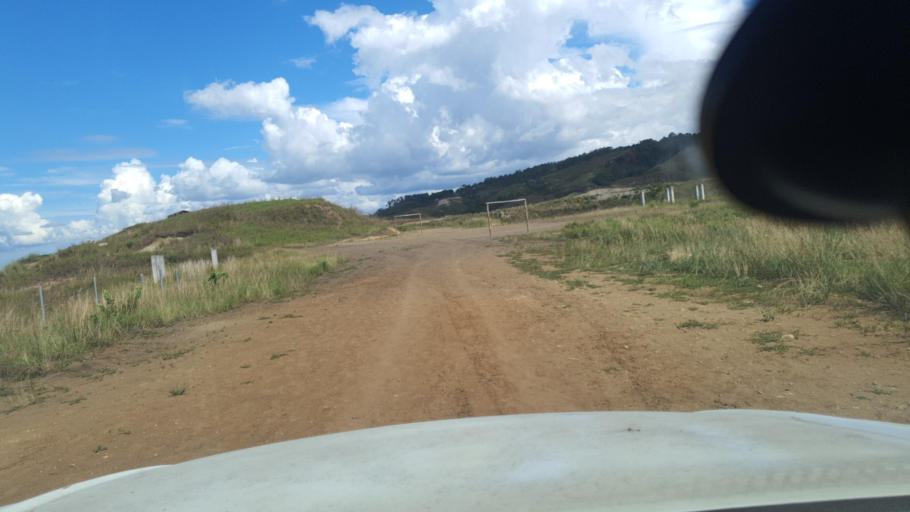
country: SB
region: Guadalcanal
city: Honiara
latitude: -9.4534
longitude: 159.9639
